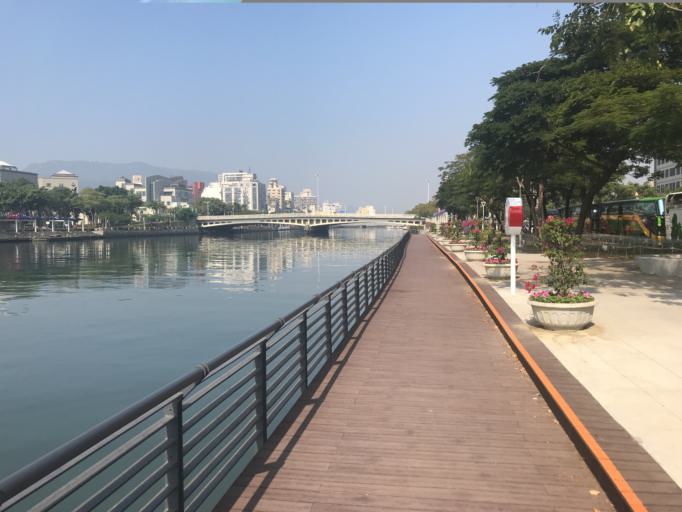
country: TW
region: Kaohsiung
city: Kaohsiung
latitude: 22.6250
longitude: 120.2896
